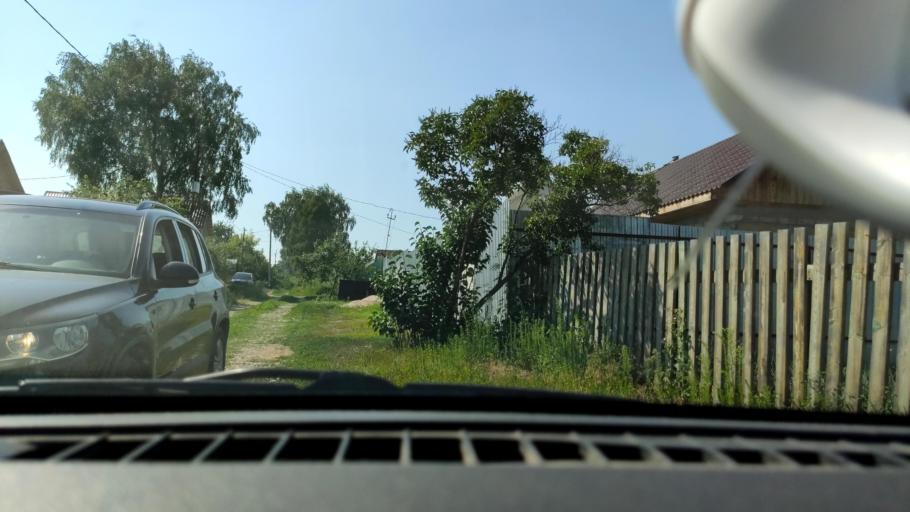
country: RU
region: Samara
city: Petra-Dubrava
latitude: 53.2681
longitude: 50.3002
